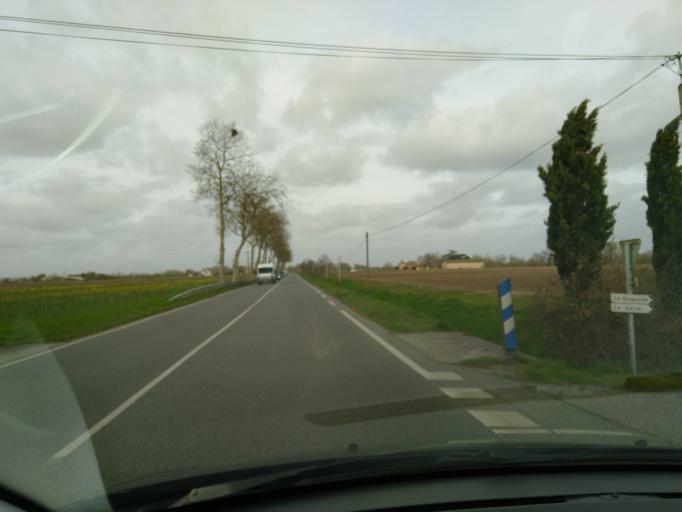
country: FR
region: Midi-Pyrenees
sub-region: Departement de la Haute-Garonne
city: Merville
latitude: 43.7392
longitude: 1.3127
